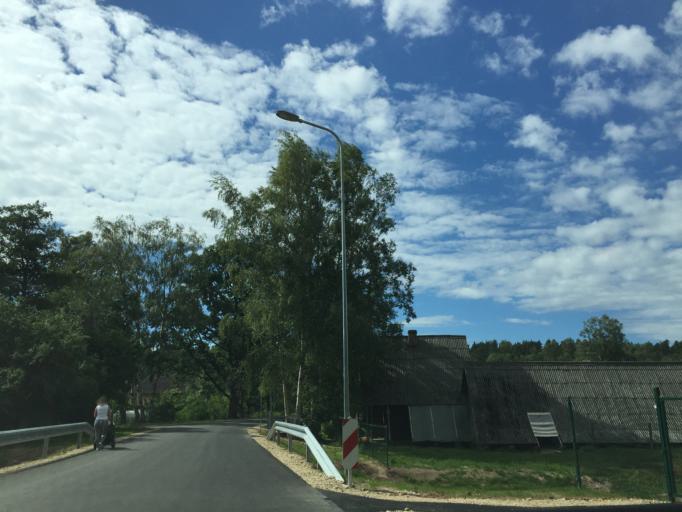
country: LV
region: Carnikava
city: Carnikava
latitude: 57.1176
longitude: 24.2273
